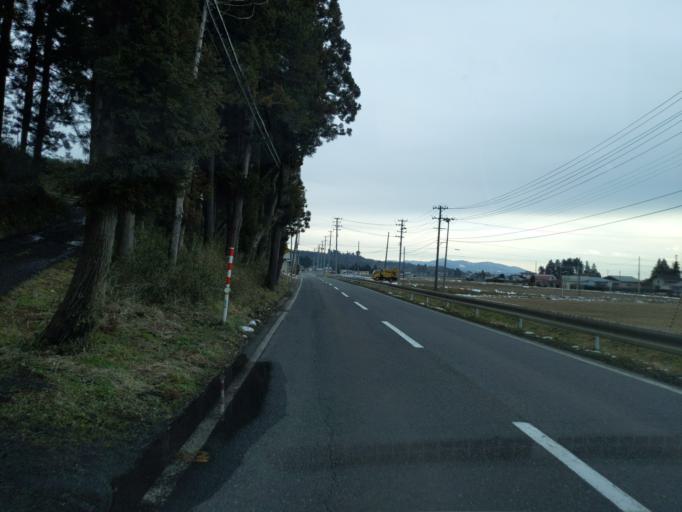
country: JP
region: Iwate
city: Mizusawa
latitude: 39.1759
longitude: 141.1920
